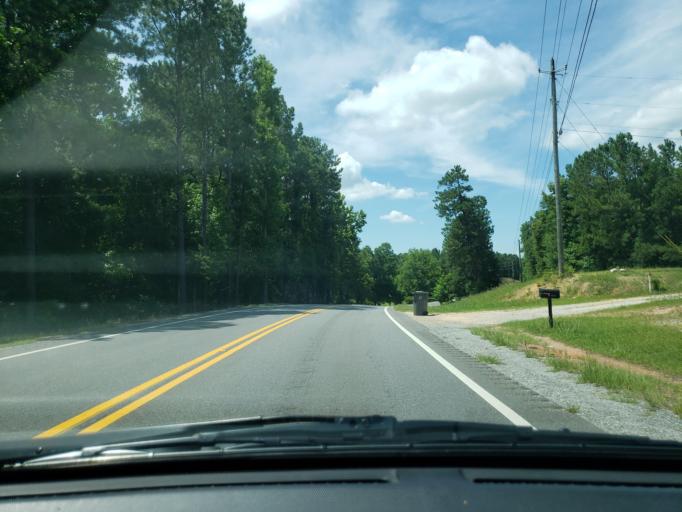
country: US
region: Alabama
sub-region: Elmore County
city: Eclectic
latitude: 32.6330
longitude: -85.9538
